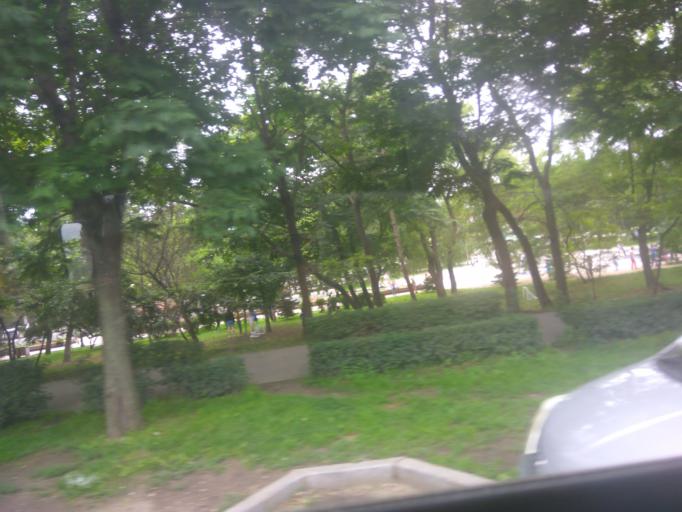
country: RU
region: Primorskiy
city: Vladivostok
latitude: 43.1631
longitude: 131.9130
